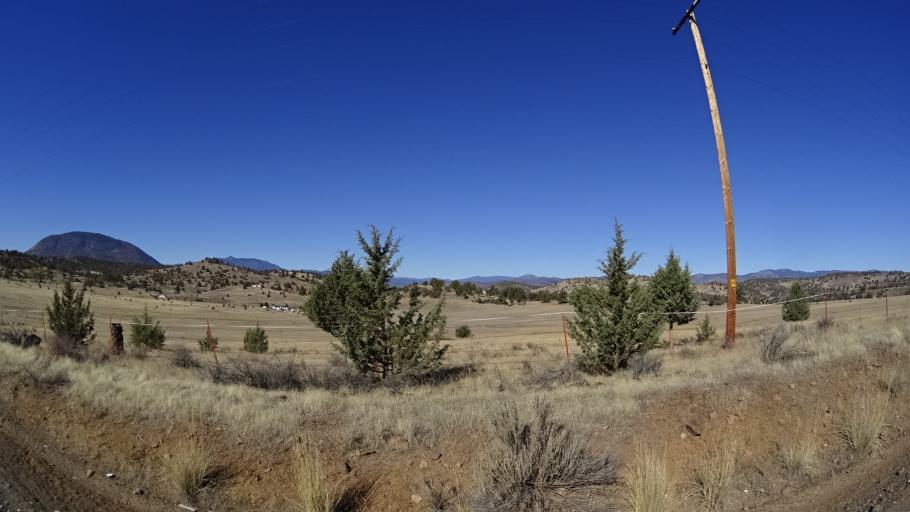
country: US
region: California
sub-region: Siskiyou County
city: Montague
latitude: 41.8804
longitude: -122.4170
